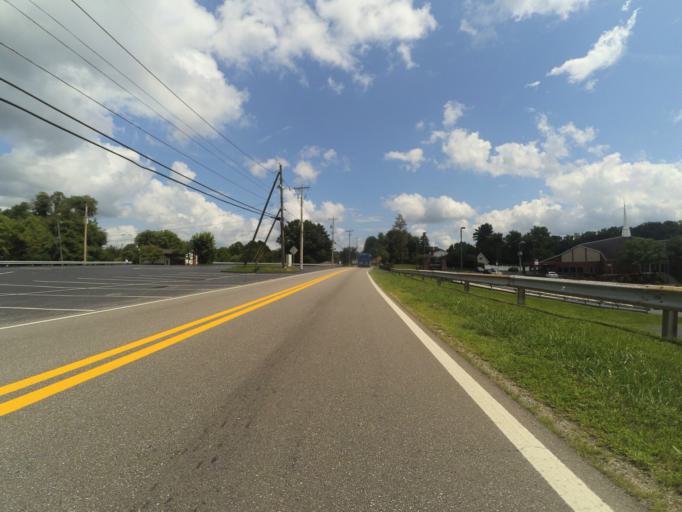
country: US
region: West Virginia
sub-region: Cabell County
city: Pea Ridge
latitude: 38.4102
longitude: -82.3388
